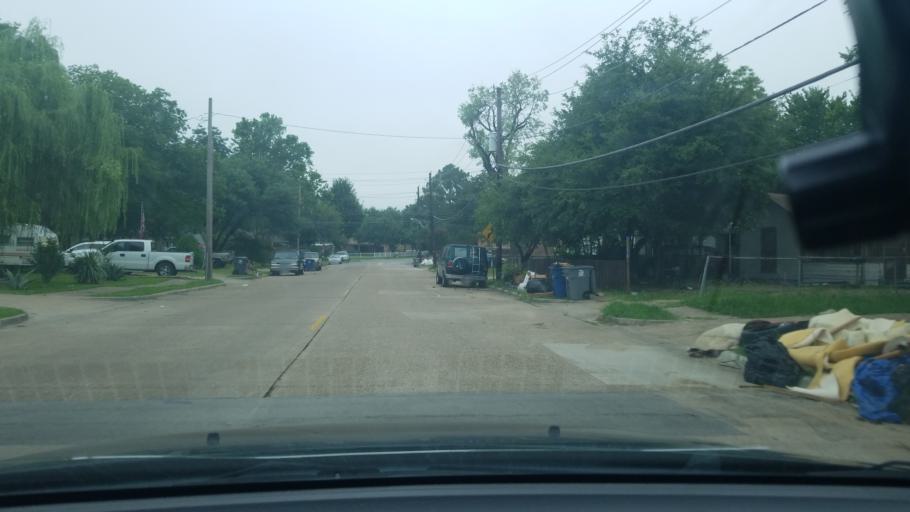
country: US
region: Texas
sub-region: Dallas County
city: Balch Springs
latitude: 32.7601
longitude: -96.6728
